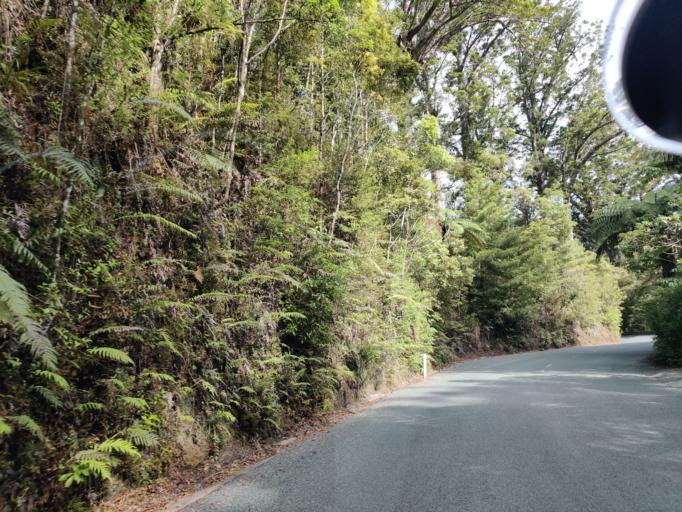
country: NZ
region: Northland
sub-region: Kaipara District
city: Dargaville
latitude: -35.6485
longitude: 173.5635
